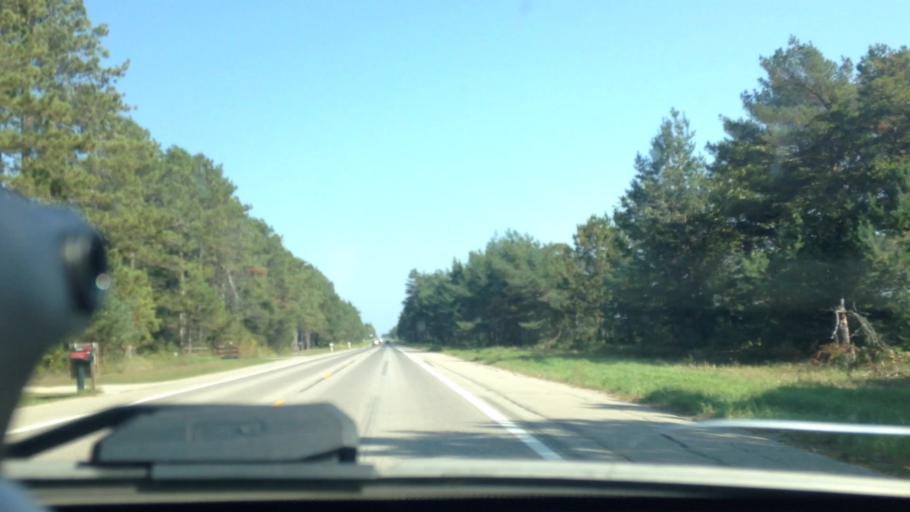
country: US
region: Michigan
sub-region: Luce County
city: Newberry
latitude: 46.3034
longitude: -85.4817
